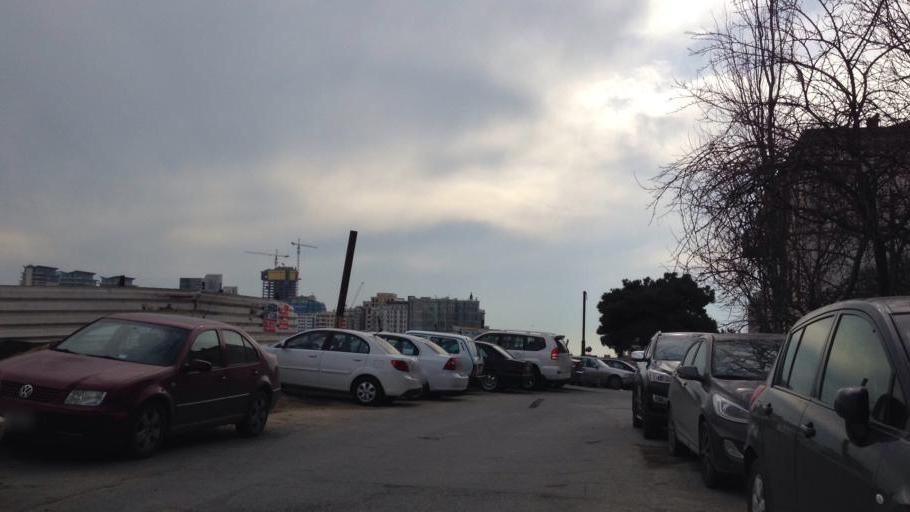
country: AZ
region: Baki
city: Baku
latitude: 40.3826
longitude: 49.8498
